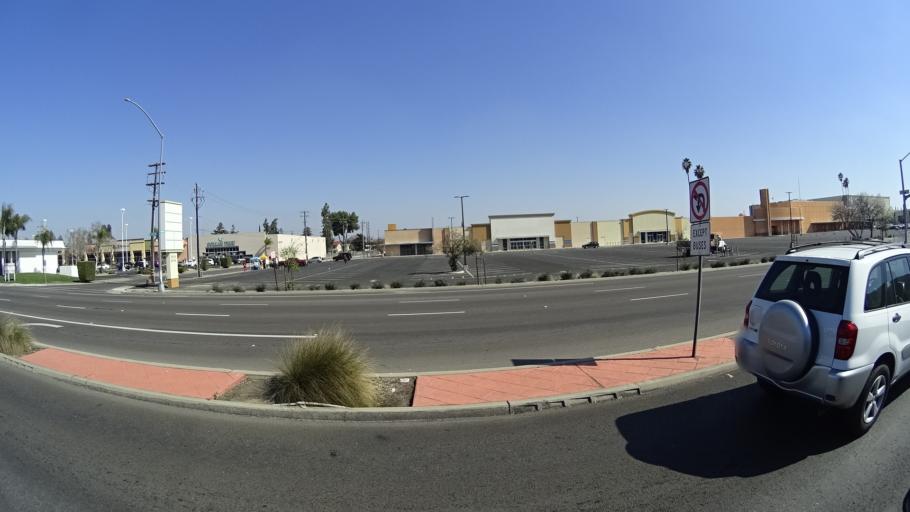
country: US
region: California
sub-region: Fresno County
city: Fresno
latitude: 36.7847
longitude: -119.7908
